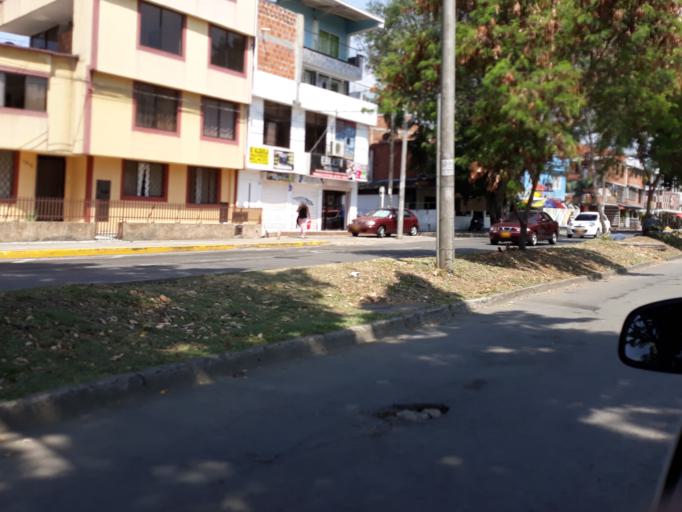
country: CO
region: Valle del Cauca
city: Cali
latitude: 3.4785
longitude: -76.4955
